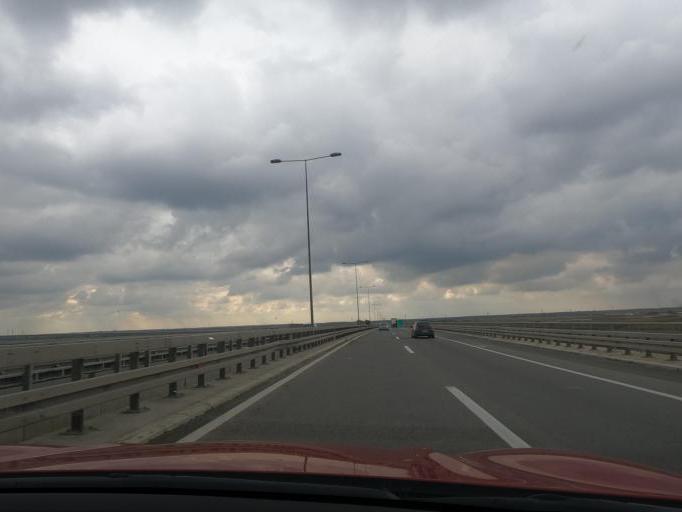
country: RS
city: Novi Banovci
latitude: 44.8883
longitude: 20.2911
